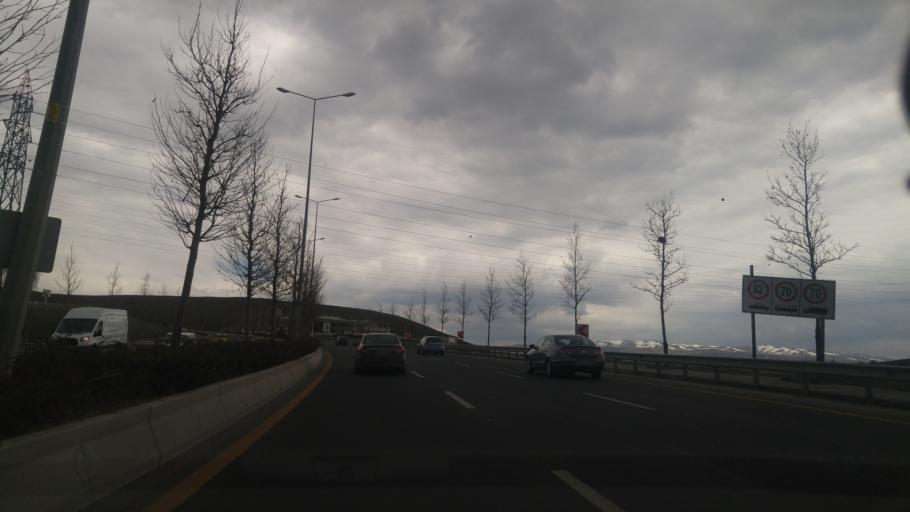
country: TR
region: Ankara
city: Mamak
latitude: 39.8855
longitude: 32.9160
